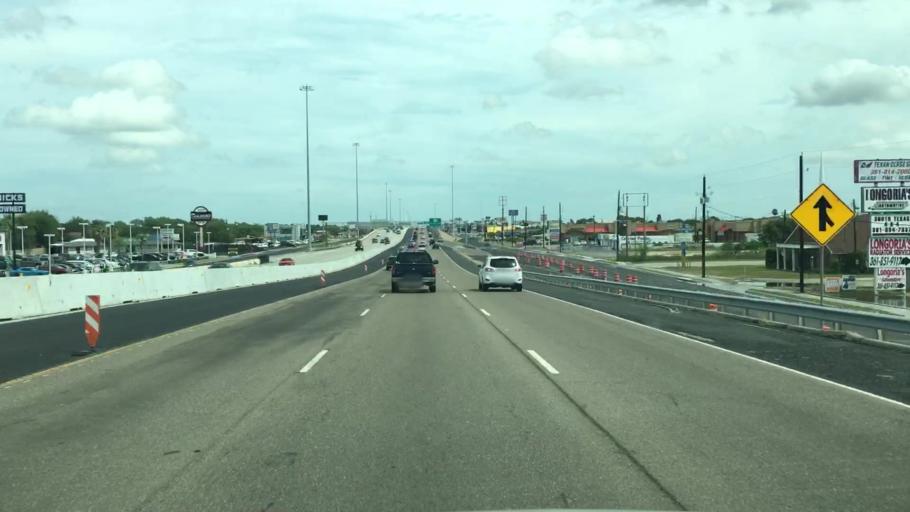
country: US
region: Texas
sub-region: Nueces County
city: Corpus Christi
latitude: 27.7278
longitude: -97.4116
